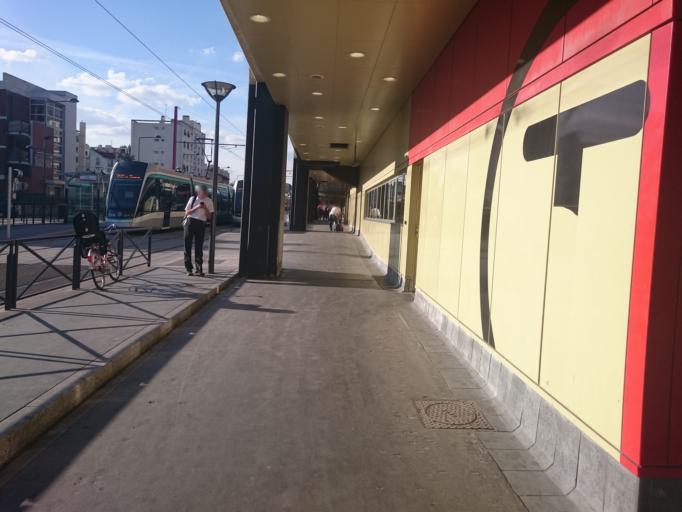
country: FR
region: Ile-de-France
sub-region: Departement du Val-de-Marne
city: Villejuif
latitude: 48.7869
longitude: 2.3671
